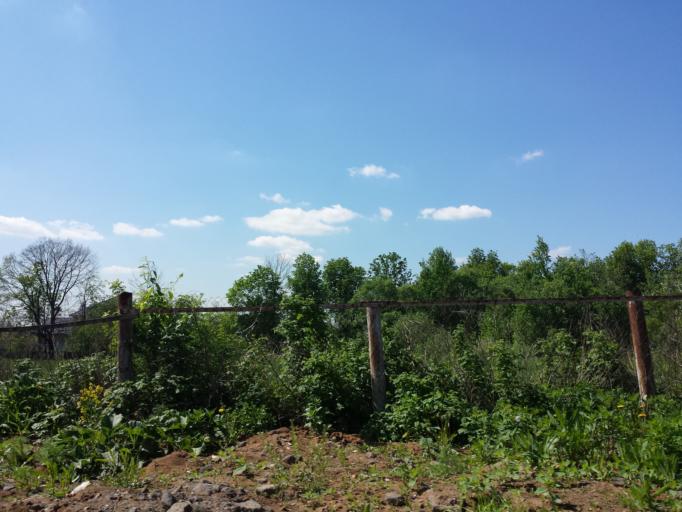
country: RU
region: Moskovskaya
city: Povedniki
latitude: 55.9304
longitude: 37.6151
